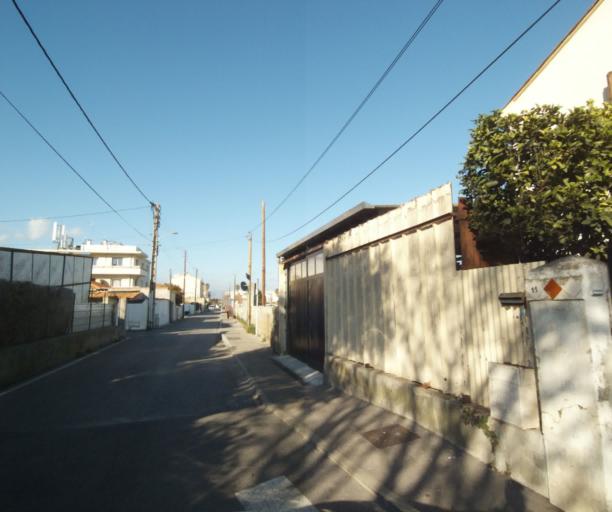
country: FR
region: Provence-Alpes-Cote d'Azur
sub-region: Departement des Alpes-Maritimes
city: Antibes
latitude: 43.5975
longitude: 7.1242
